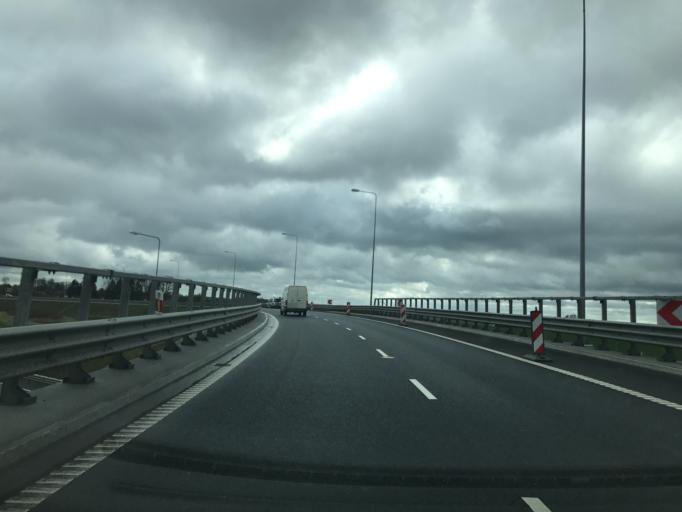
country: PL
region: Warmian-Masurian Voivodeship
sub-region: Powiat olsztynski
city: Olsztynek
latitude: 53.5830
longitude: 20.2521
